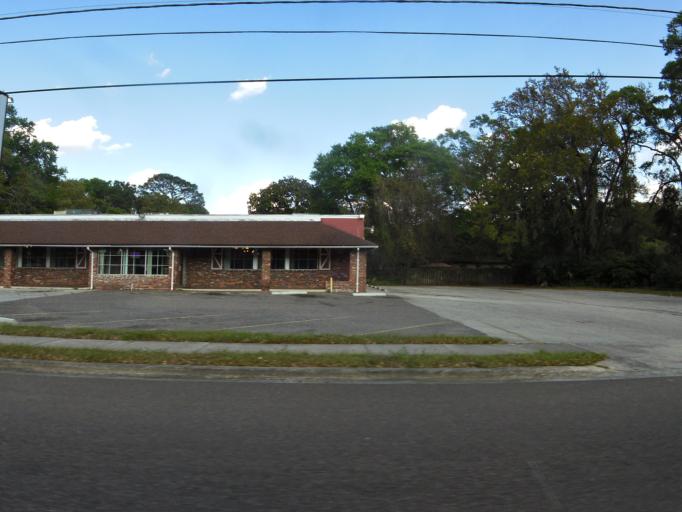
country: US
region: Florida
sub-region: Duval County
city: Jacksonville
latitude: 30.3322
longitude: -81.5970
